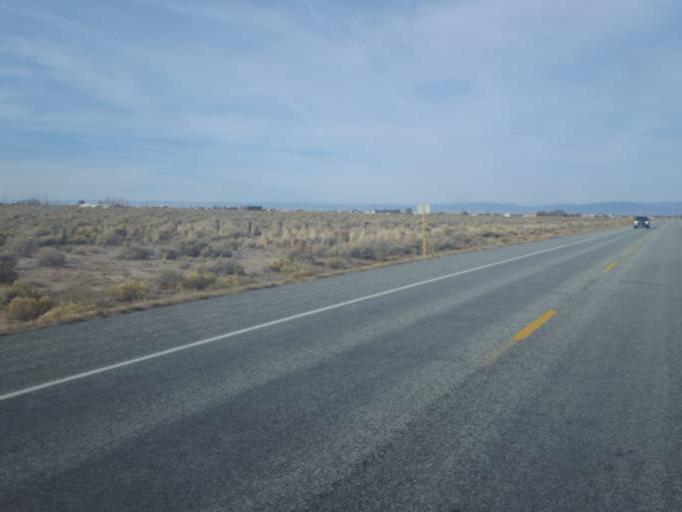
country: US
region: Colorado
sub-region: Alamosa County
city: Alamosa East
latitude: 37.4747
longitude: -105.6940
